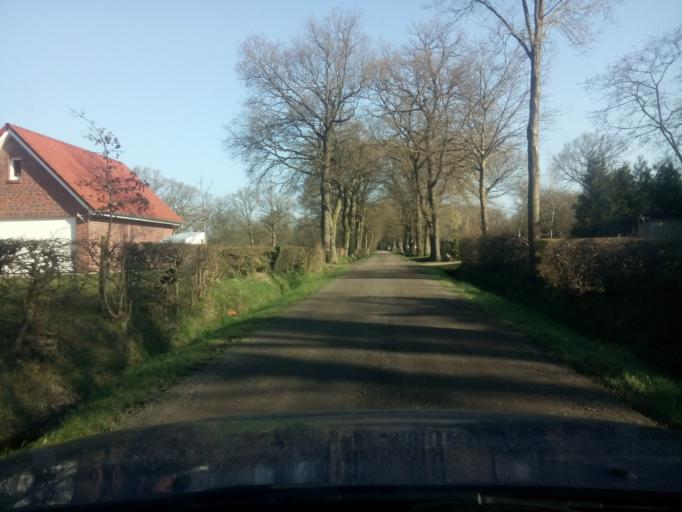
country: DE
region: Lower Saxony
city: Osterholz-Scharmbeck
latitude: 53.2241
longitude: 8.7556
